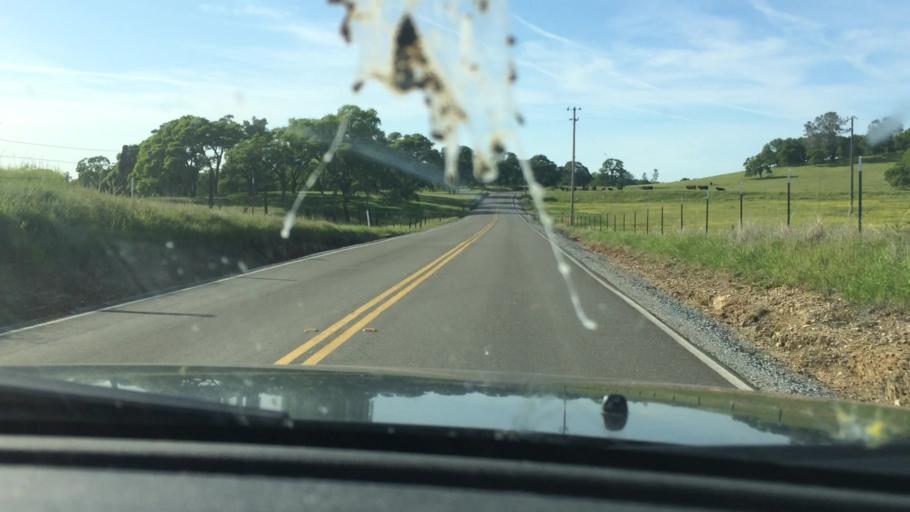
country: US
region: California
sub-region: Amador County
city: Plymouth
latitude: 38.4972
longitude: -120.9386
